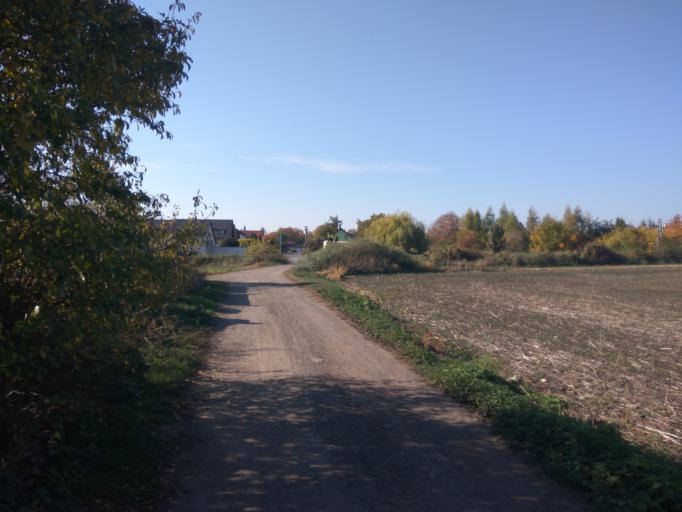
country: CZ
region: Central Bohemia
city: Hovorcovice
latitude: 50.1773
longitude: 14.5280
